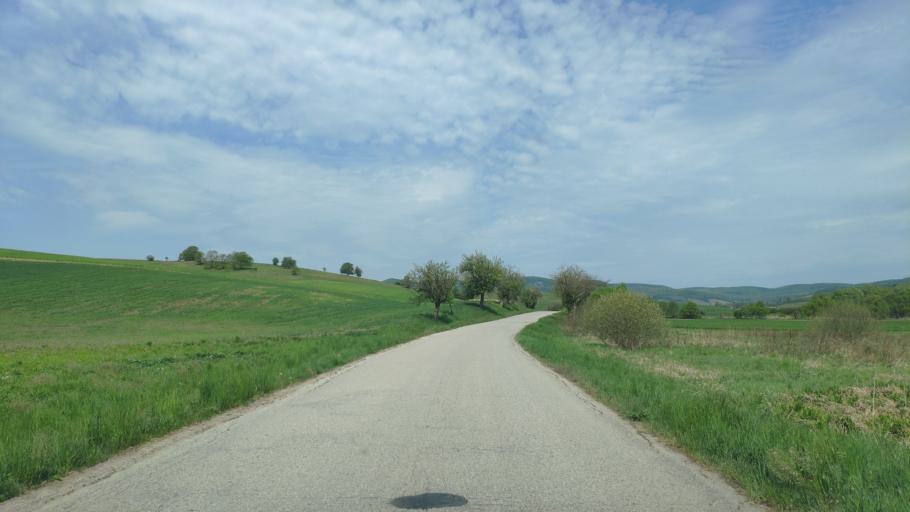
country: SK
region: Banskobystricky
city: Rimavska Sobota
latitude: 48.4261
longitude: 20.2138
